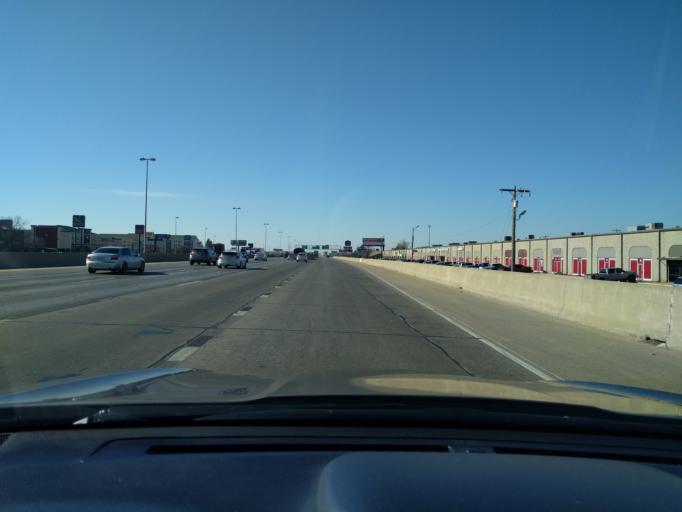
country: US
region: Oklahoma
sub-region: Oklahoma County
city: Warr Acres
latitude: 35.4603
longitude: -97.5932
